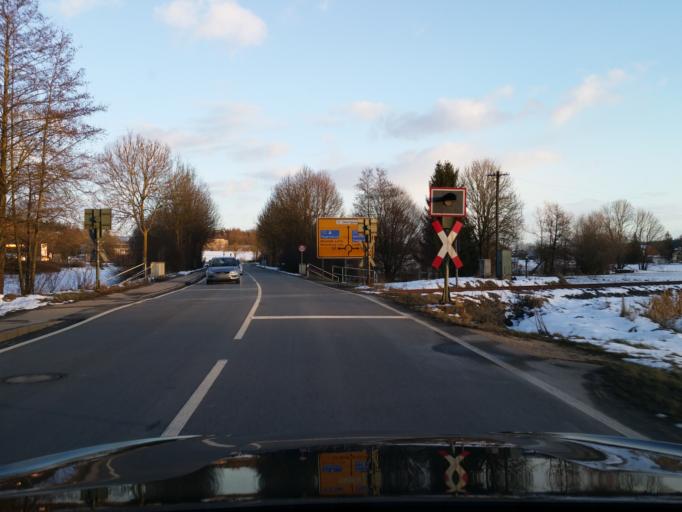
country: DE
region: Bavaria
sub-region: Lower Bavaria
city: Weihmichl
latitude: 48.5841
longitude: 12.0614
